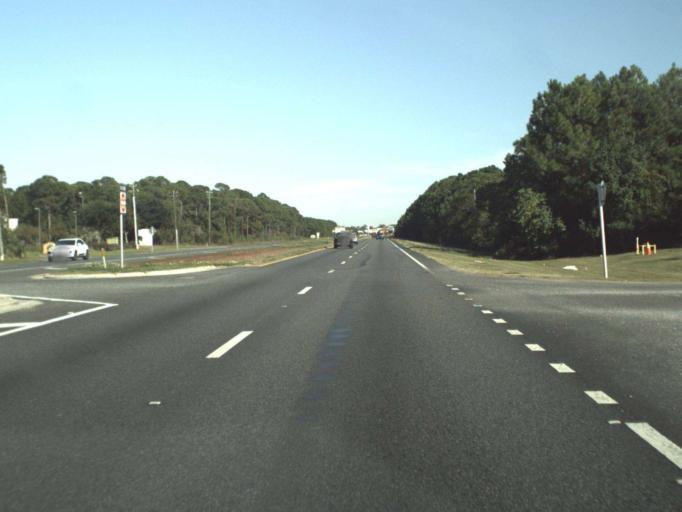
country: US
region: Florida
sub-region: Walton County
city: Miramar Beach
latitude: 30.3849
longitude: -86.3771
